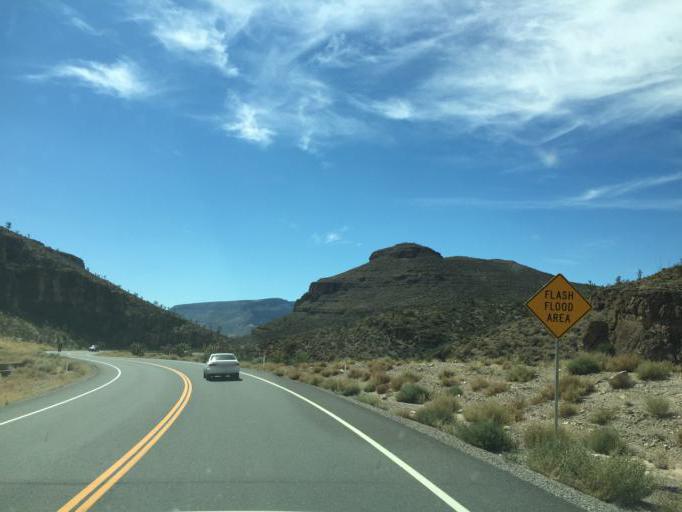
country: US
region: Arizona
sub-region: Mohave County
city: Meadview
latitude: 35.9000
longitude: -113.9421
